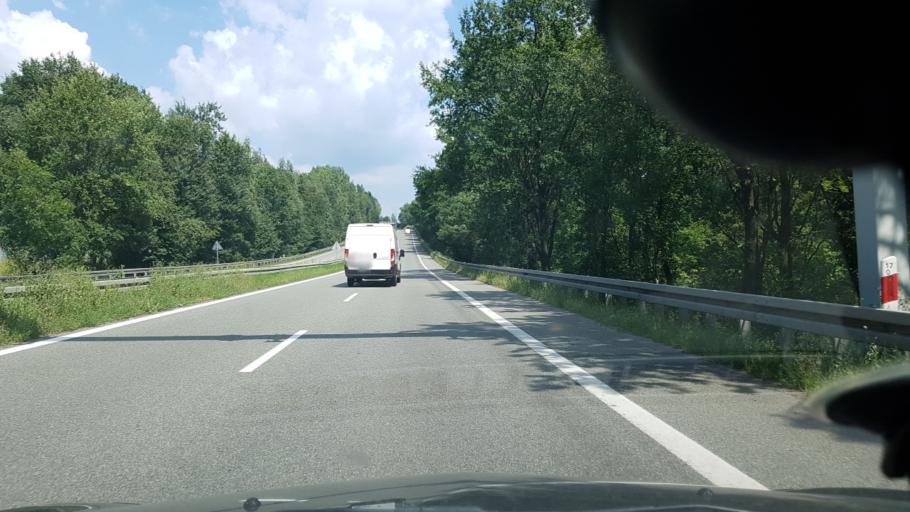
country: PL
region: Silesian Voivodeship
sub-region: Powiat mikolowski
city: Laziska Gorne
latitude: 50.1440
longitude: 18.8450
